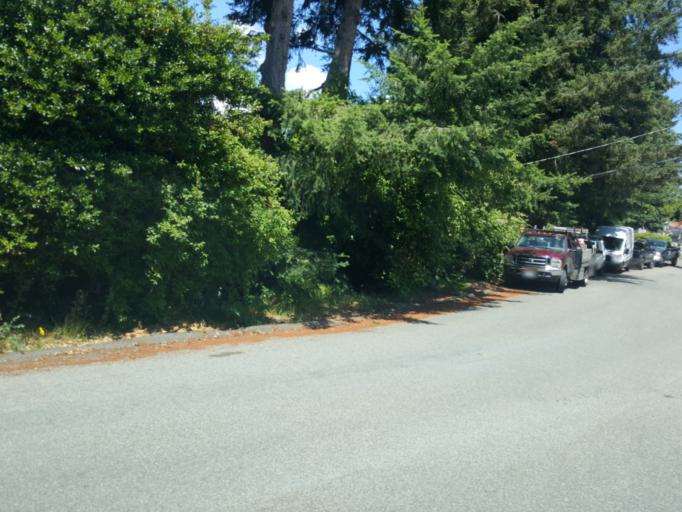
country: US
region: Washington
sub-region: Pierce County
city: University Place
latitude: 47.2166
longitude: -122.5694
